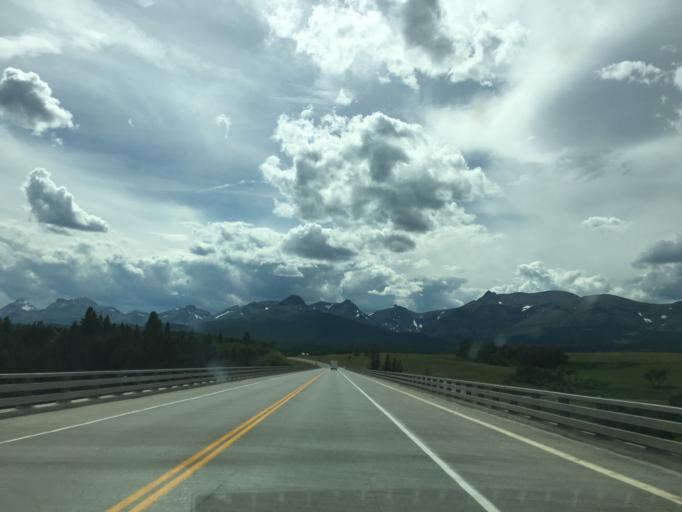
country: US
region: Montana
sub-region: Glacier County
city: South Browning
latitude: 48.4504
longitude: -113.2038
